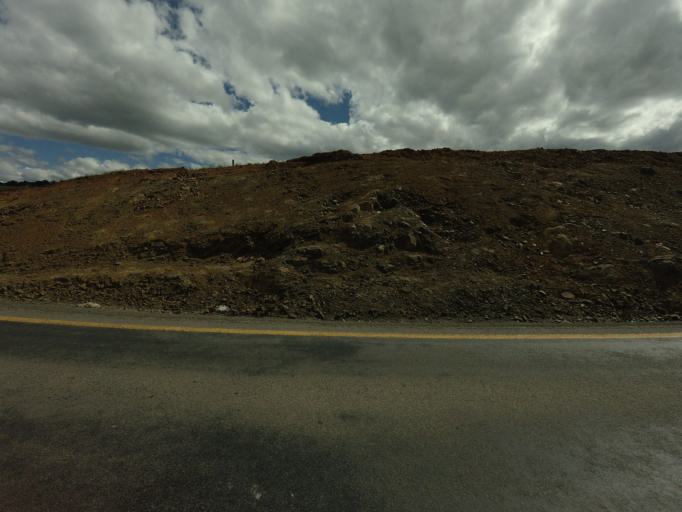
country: AU
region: Tasmania
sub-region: Brighton
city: Bridgewater
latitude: -42.2100
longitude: 147.4056
